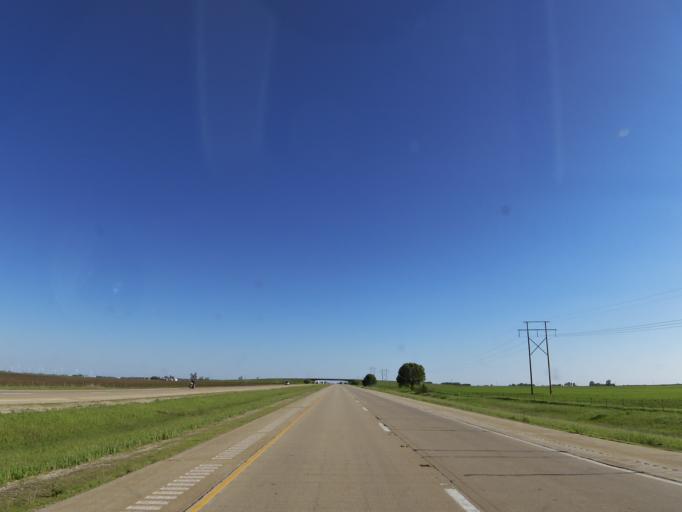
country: US
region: Illinois
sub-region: Woodford County
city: Minonk
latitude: 40.9618
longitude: -89.0566
